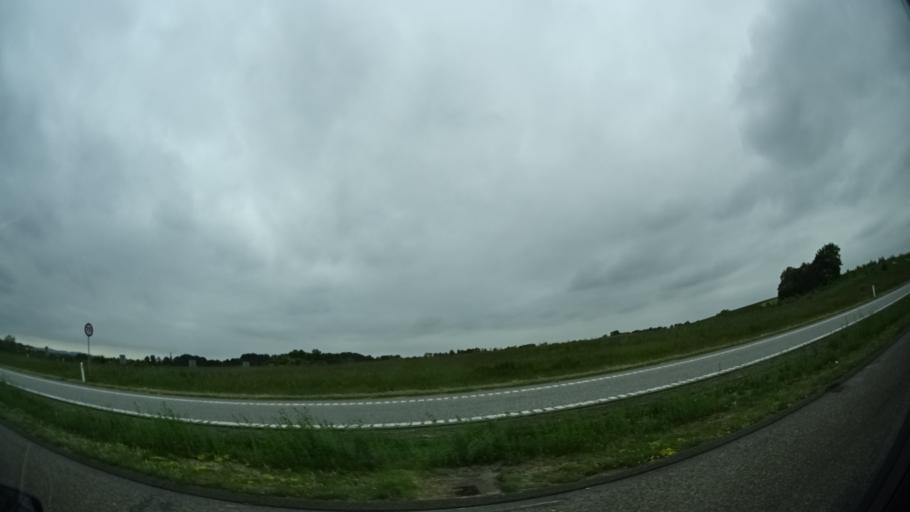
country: DK
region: Central Jutland
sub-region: Arhus Kommune
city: Framlev
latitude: 56.1591
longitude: 10.0453
